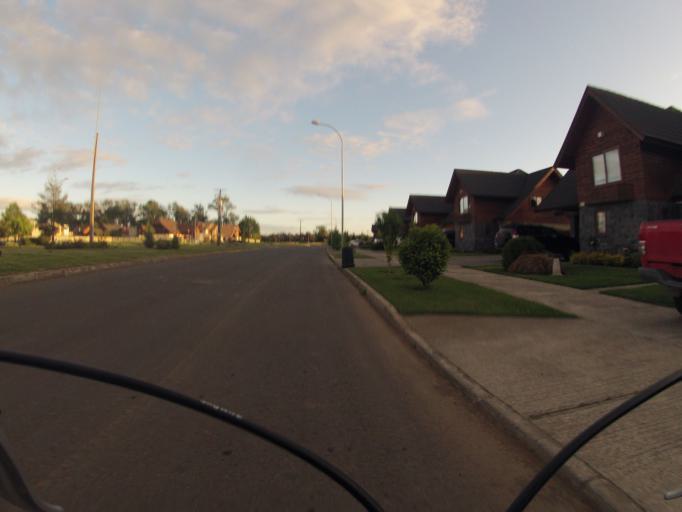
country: CL
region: Araucania
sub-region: Provincia de Cautin
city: Temuco
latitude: -38.7422
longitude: -72.6496
